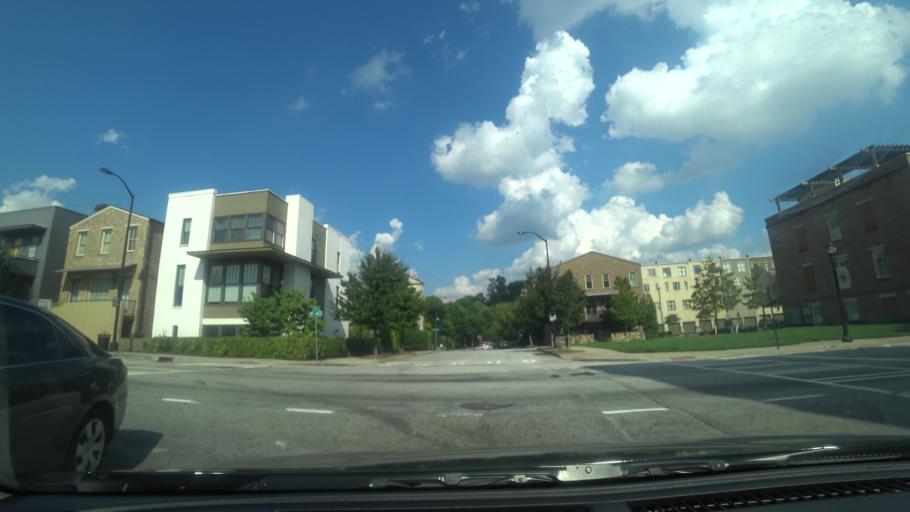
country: US
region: Georgia
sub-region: Fulton County
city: Atlanta
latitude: 33.7405
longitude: -84.3580
